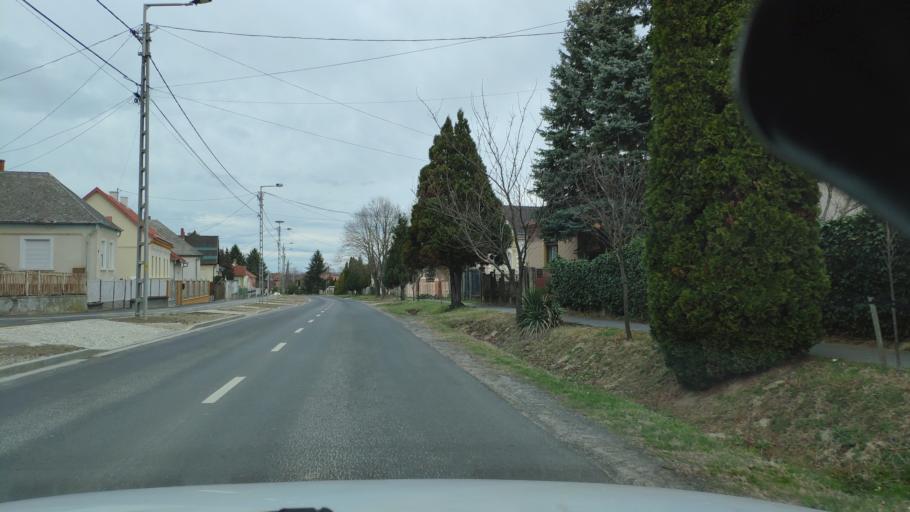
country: HU
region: Zala
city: Zalakomar
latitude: 46.5621
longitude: 17.1237
